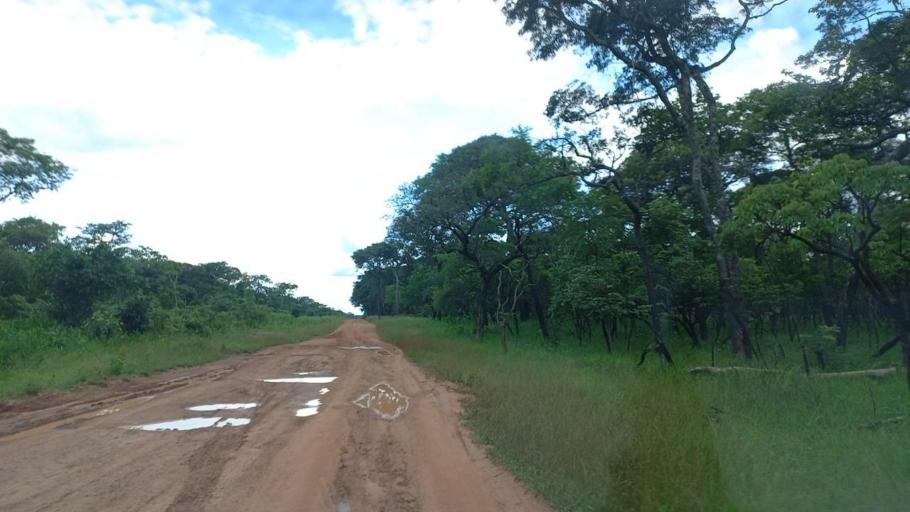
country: ZM
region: North-Western
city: Mwinilunga
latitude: -11.8072
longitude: 24.3688
